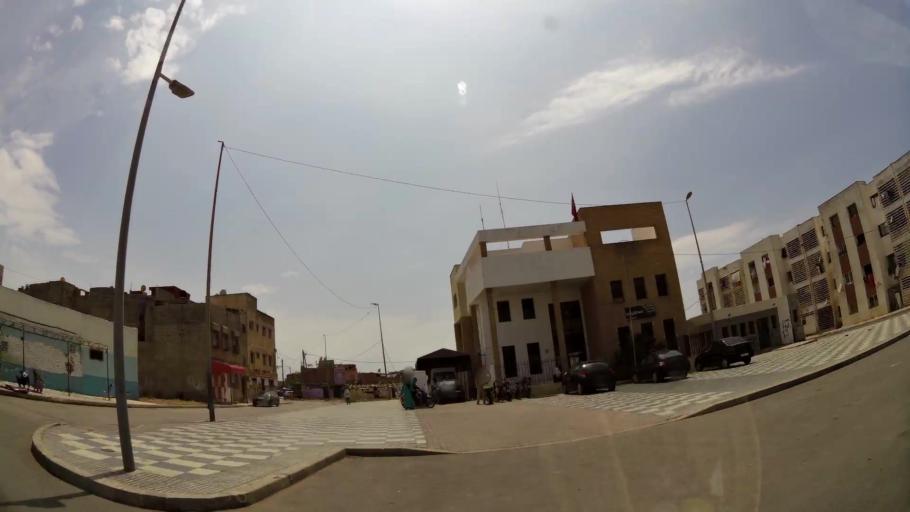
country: MA
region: Rabat-Sale-Zemmour-Zaer
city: Sale
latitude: 34.0577
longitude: -6.8162
